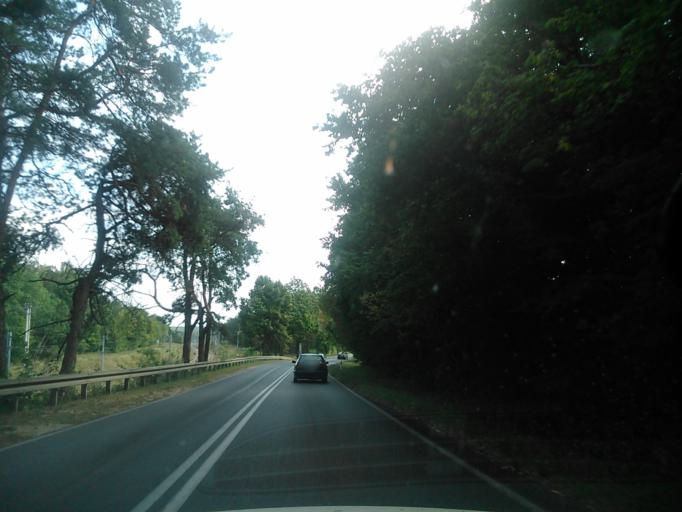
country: PL
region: Warmian-Masurian Voivodeship
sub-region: Powiat dzialdowski
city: Ilowo -Osada
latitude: 53.1569
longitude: 20.3138
